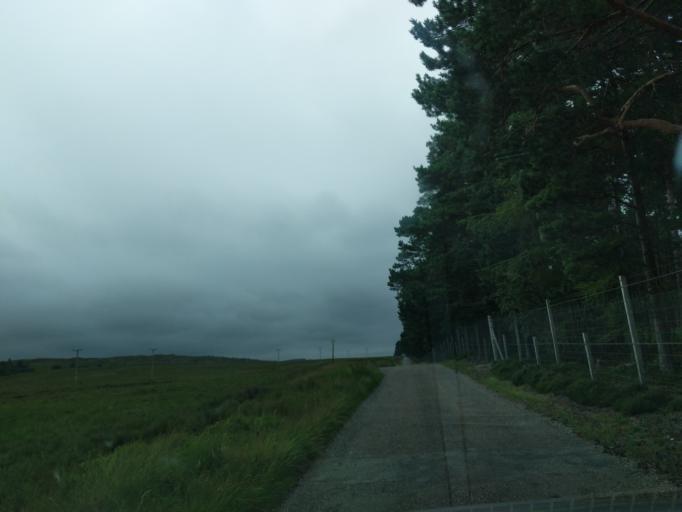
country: GB
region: Scotland
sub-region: Highland
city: Grantown on Spey
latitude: 57.3998
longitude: -3.7088
